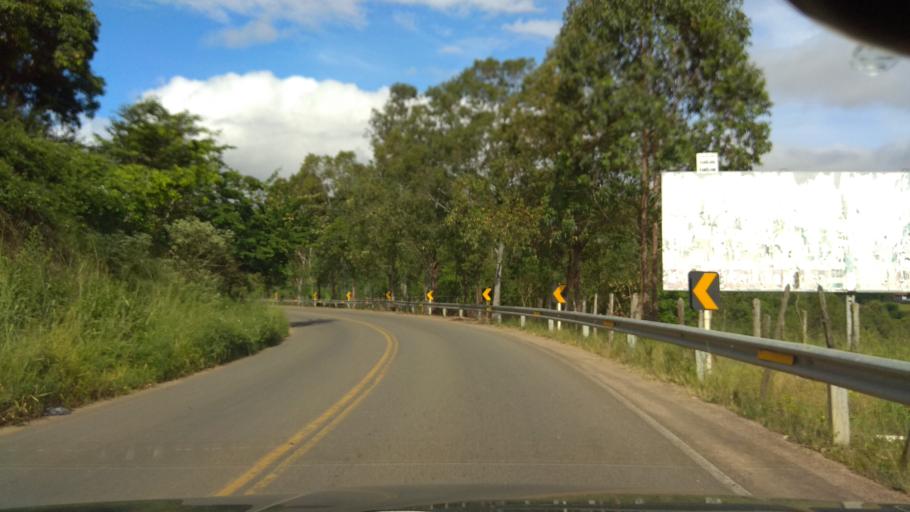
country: BR
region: Bahia
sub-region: Ubaira
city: Ubaira
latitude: -13.2593
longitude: -39.6647
